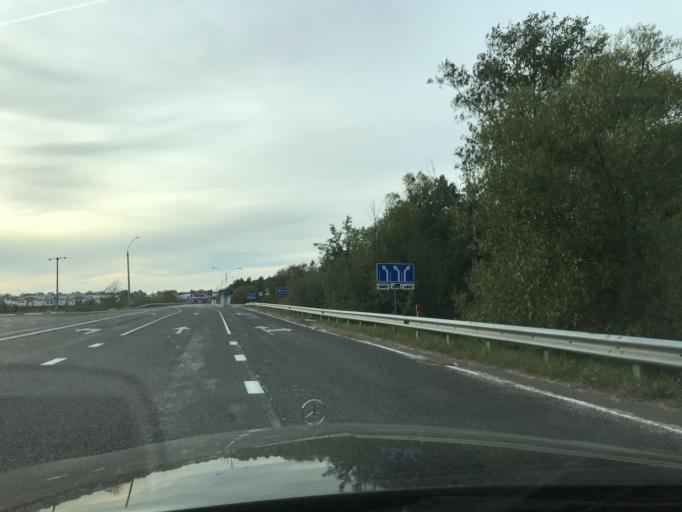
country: PL
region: Lublin Voivodeship
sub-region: Powiat bialski
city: Slawatycze
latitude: 51.7610
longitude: 23.6095
